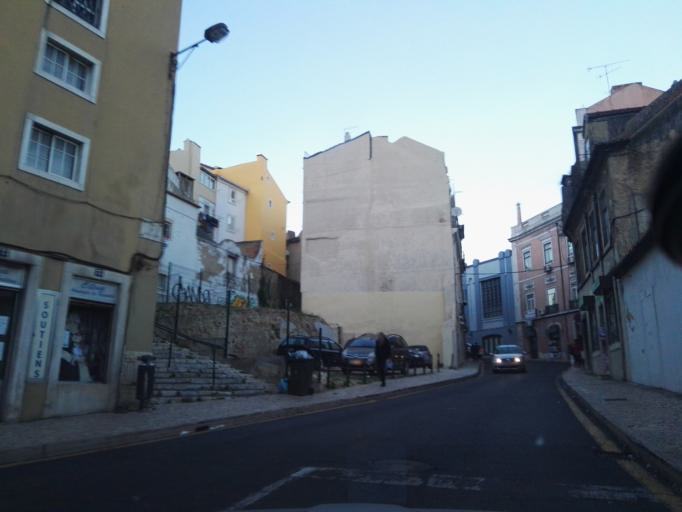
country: PT
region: Lisbon
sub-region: Lisbon
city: Lisbon
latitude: 38.7178
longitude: -9.1367
